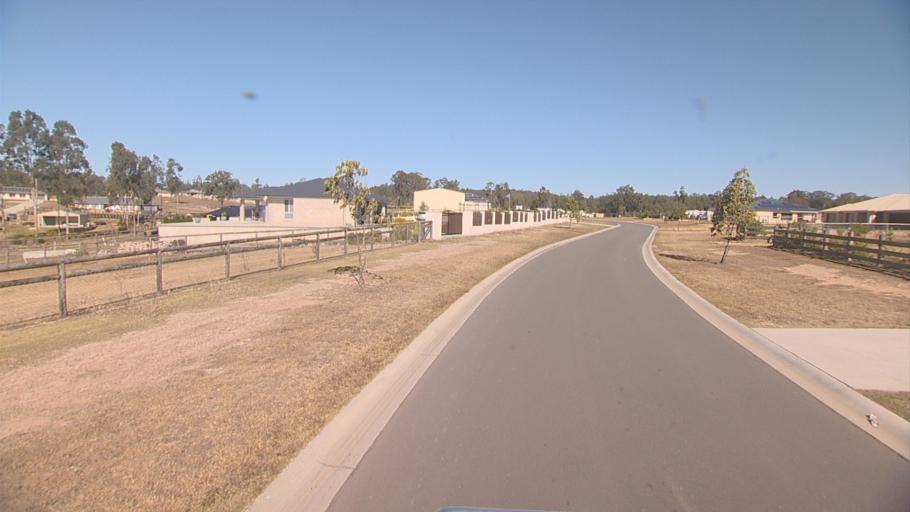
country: AU
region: Queensland
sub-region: Logan
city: Cedar Vale
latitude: -27.8706
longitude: 153.0456
